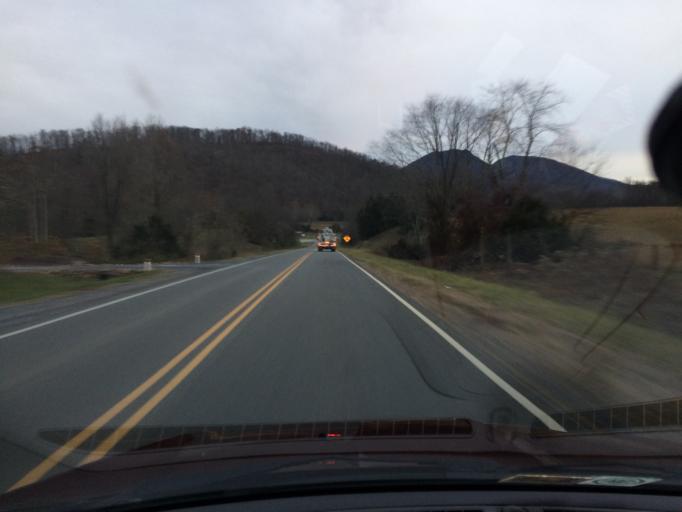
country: US
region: Virginia
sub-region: City of Lexington
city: Lexington
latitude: 37.8512
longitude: -79.4816
